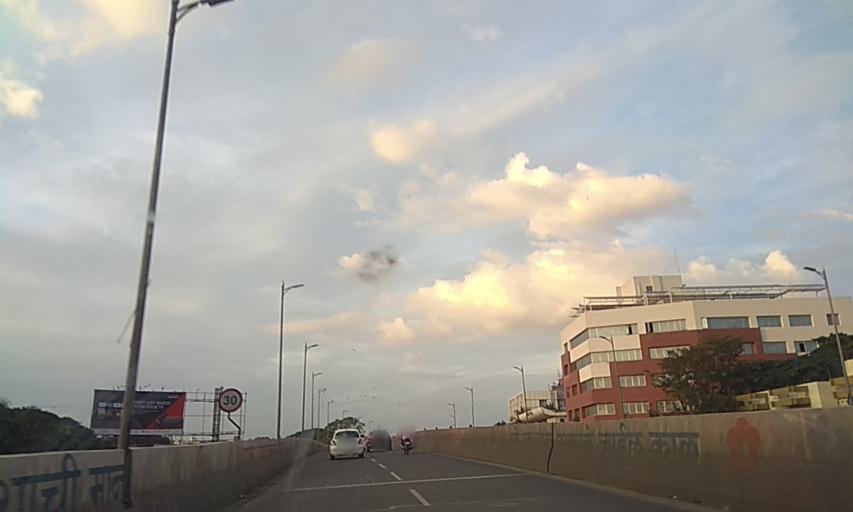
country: IN
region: Maharashtra
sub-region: Pune Division
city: Pune
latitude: 18.4957
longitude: 73.8577
